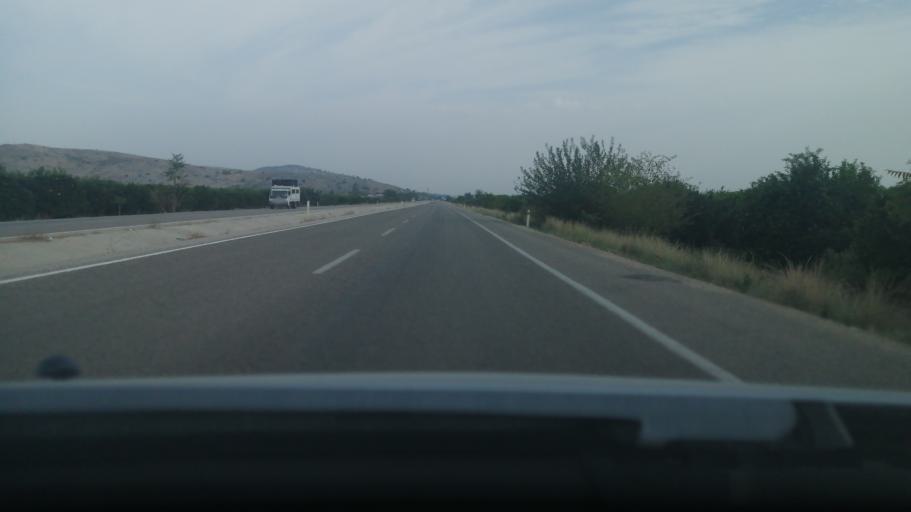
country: TR
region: Adana
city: Kozan
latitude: 37.3840
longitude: 35.8114
